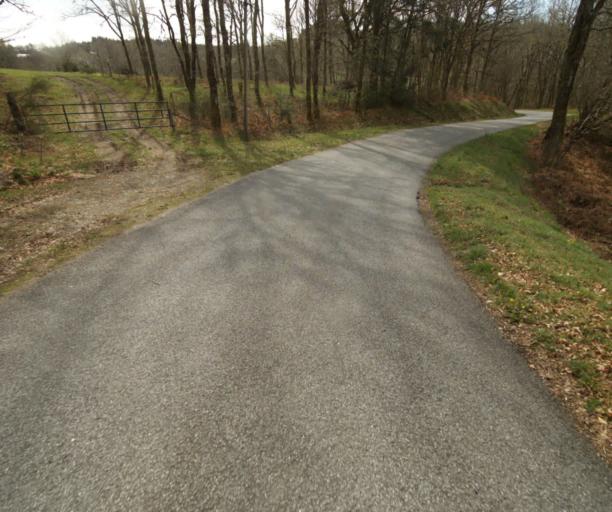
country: FR
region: Limousin
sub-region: Departement de la Correze
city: Correze
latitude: 45.3816
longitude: 1.8946
